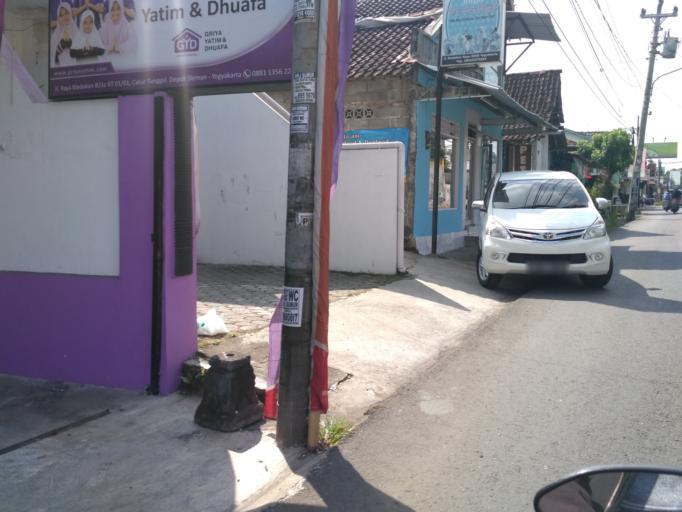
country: ID
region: Daerah Istimewa Yogyakarta
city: Depok
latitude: -7.7770
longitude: 110.4084
